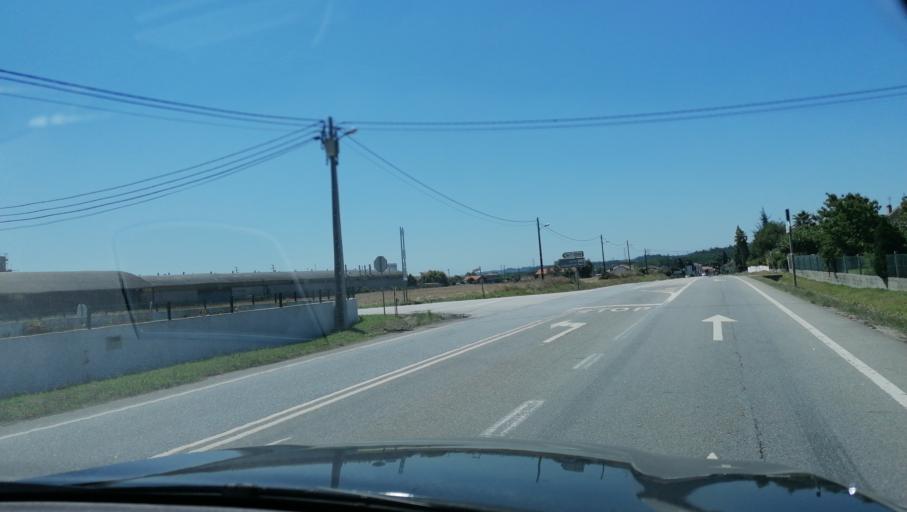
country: PT
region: Aveiro
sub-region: Anadia
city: Sangalhos
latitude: 40.4857
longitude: -8.4485
